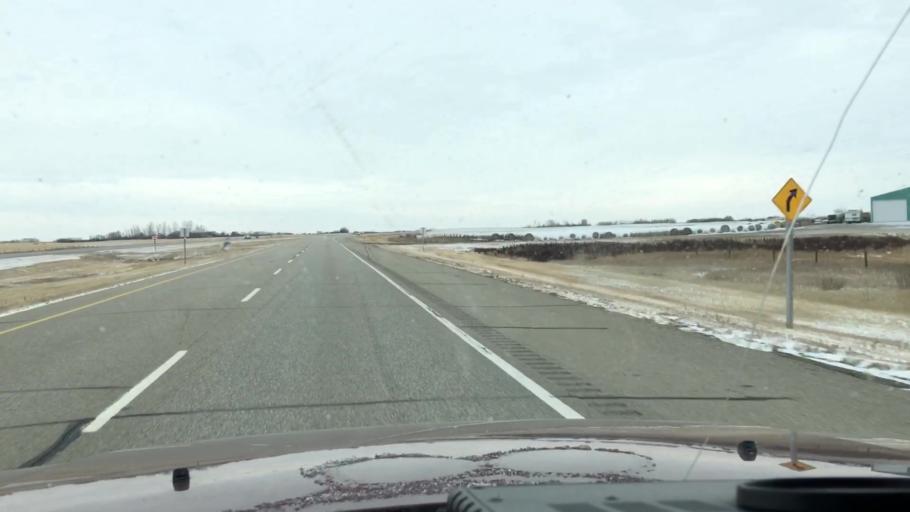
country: CA
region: Saskatchewan
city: Watrous
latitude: 51.3659
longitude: -106.1321
